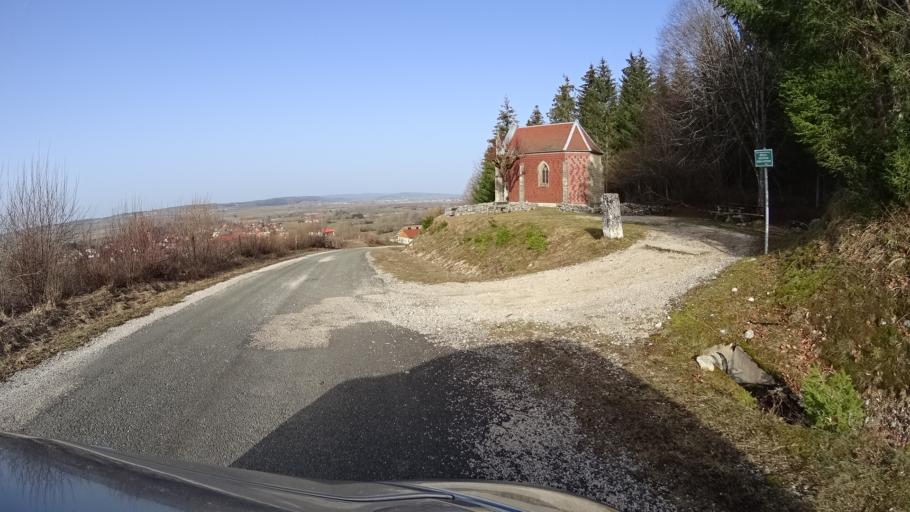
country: FR
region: Franche-Comte
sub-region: Departement du Doubs
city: Pontarlier
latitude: 46.8711
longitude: 6.2668
